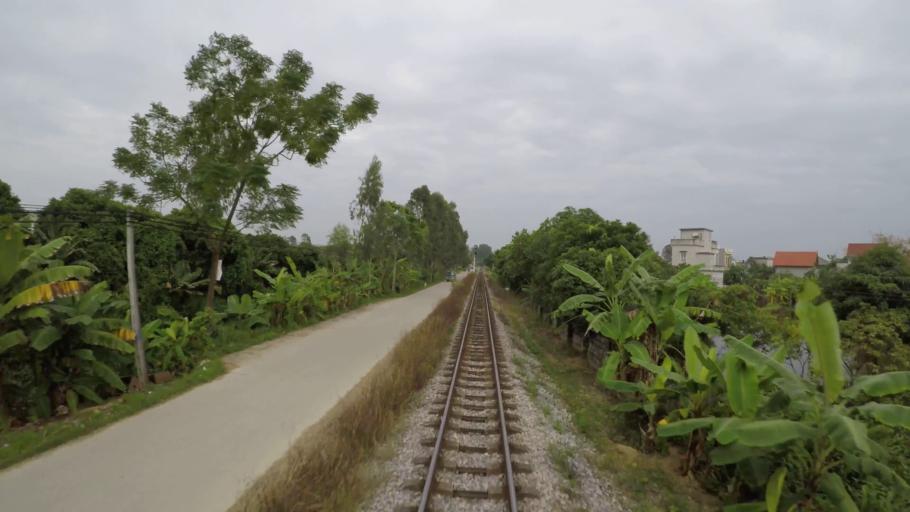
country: VN
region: Hai Duong
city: Lai Cach
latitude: 20.9494
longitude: 106.2479
